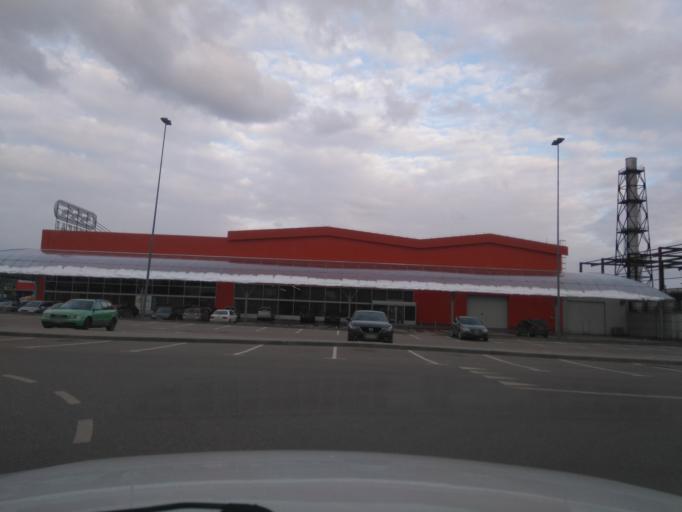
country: LT
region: Kauno apskritis
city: Dainava (Kaunas)
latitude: 54.9085
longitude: 23.9852
